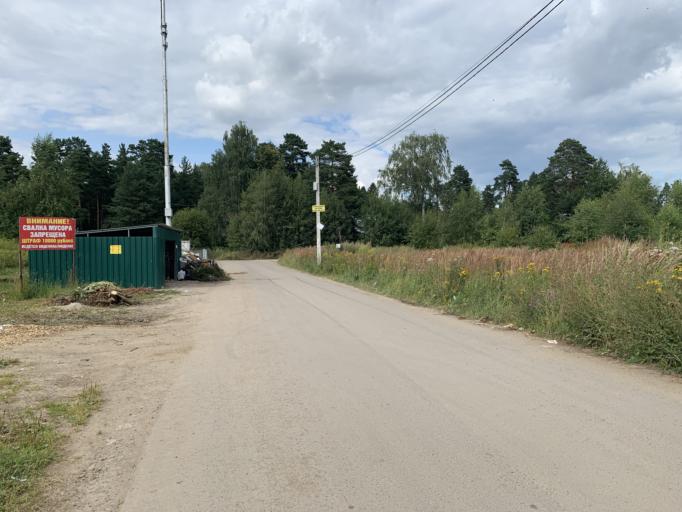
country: RU
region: Moskovskaya
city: Cherkizovo
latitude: 55.9899
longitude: 37.8011
